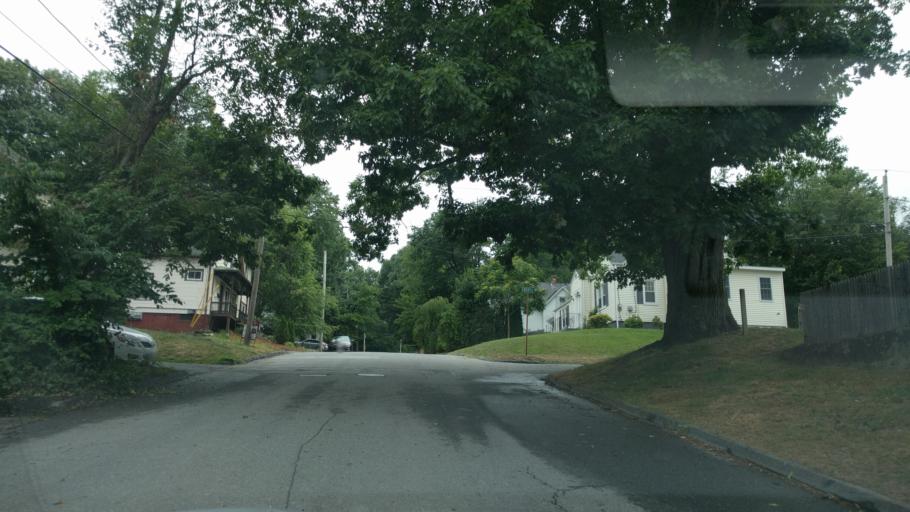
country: US
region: Massachusetts
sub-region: Worcester County
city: Sunderland
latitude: 42.2472
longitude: -71.7618
